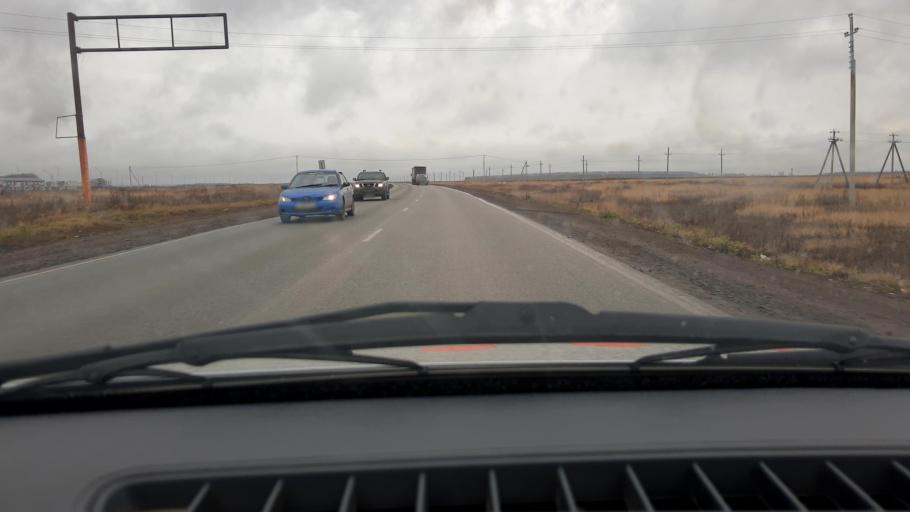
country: RU
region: Bashkortostan
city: Iglino
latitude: 54.7644
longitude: 56.2654
